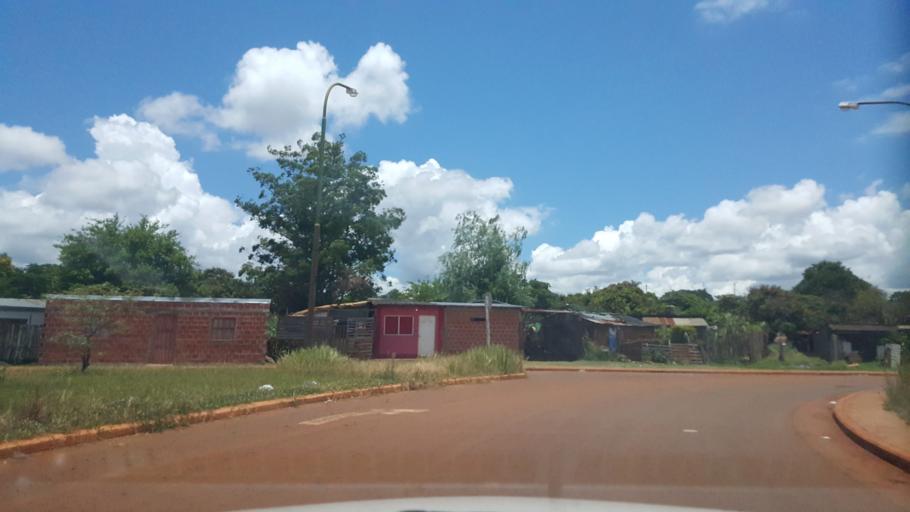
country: AR
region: Misiones
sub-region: Departamento de Capital
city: Posadas
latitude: -27.4232
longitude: -55.8904
